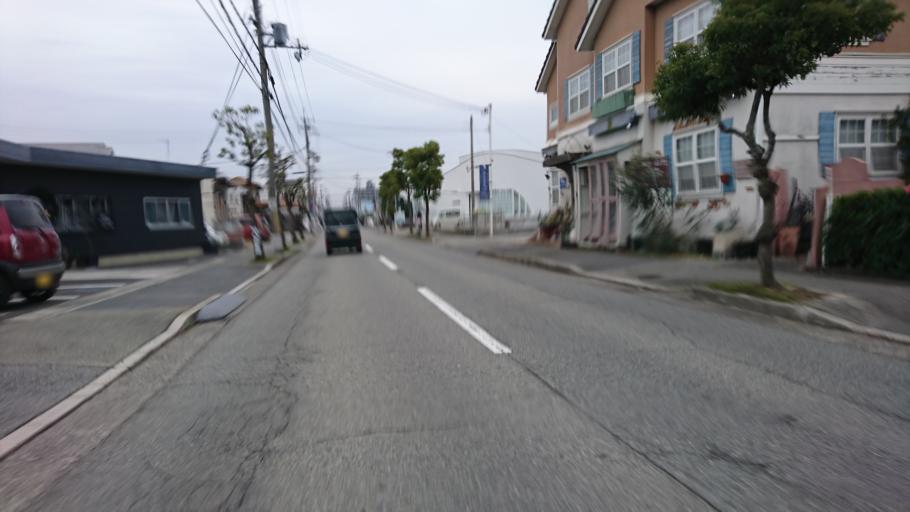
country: JP
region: Hyogo
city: Kakogawacho-honmachi
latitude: 34.7646
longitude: 134.8186
